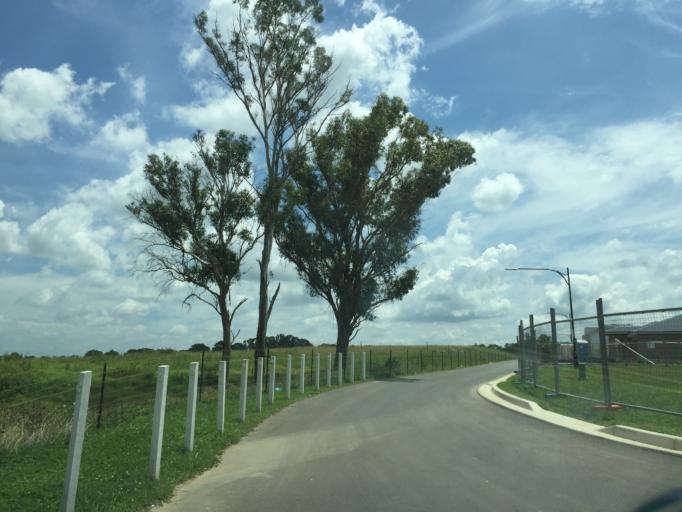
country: AU
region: New South Wales
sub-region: Blacktown
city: Quakers Hill
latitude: -33.7075
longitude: 150.8827
